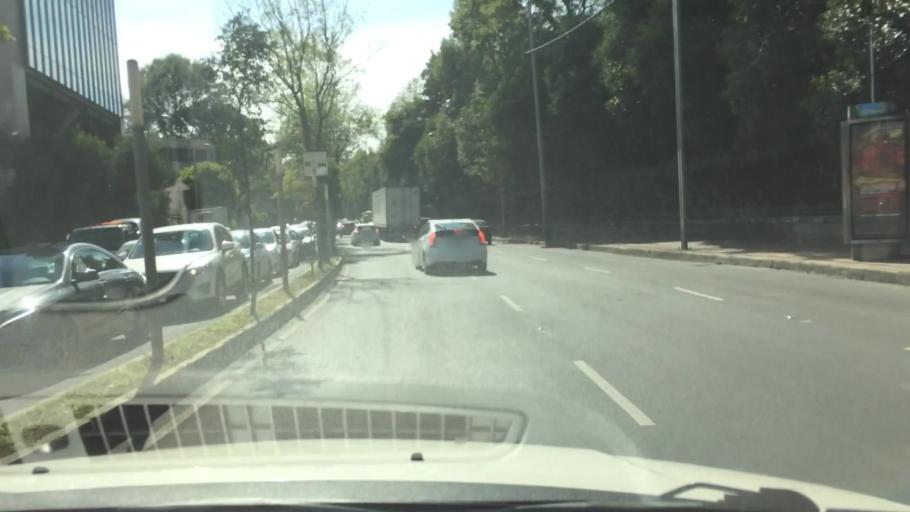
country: MX
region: Mexico City
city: Polanco
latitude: 19.4162
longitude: -99.1827
